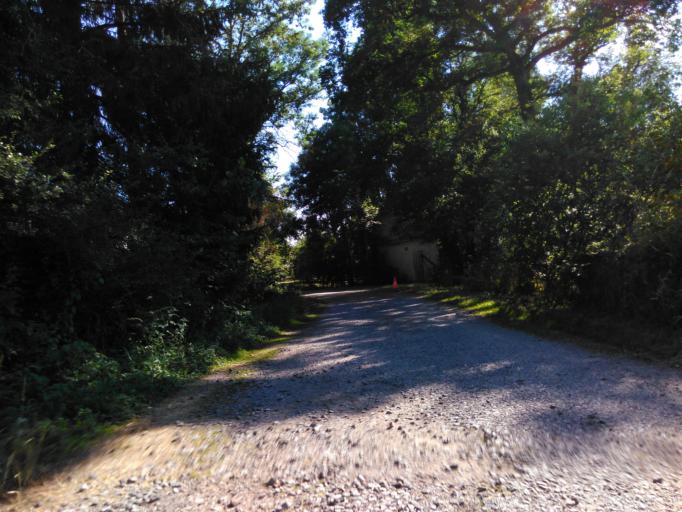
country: LU
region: Luxembourg
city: Belvaux
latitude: 49.5248
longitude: 5.9261
